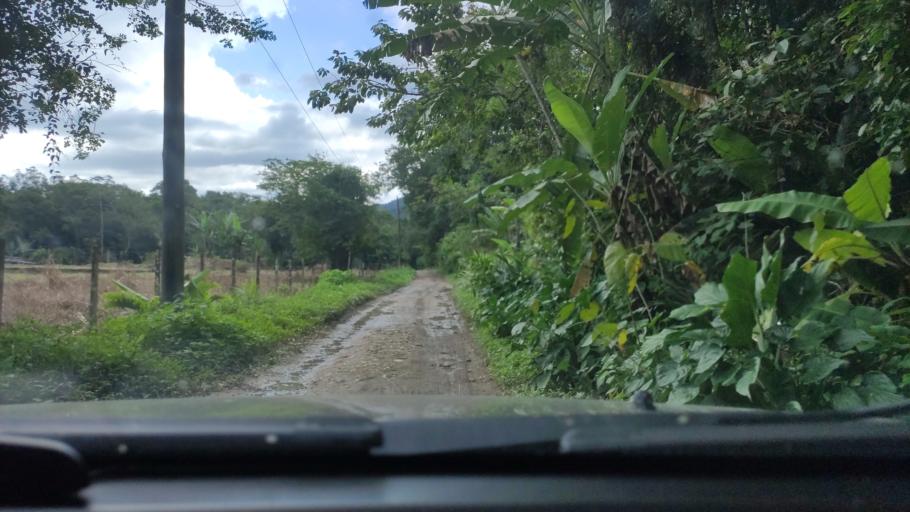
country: BR
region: Sao Paulo
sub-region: Sao Sebastiao
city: Sao Sebastiao
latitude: -23.7322
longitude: -45.4932
